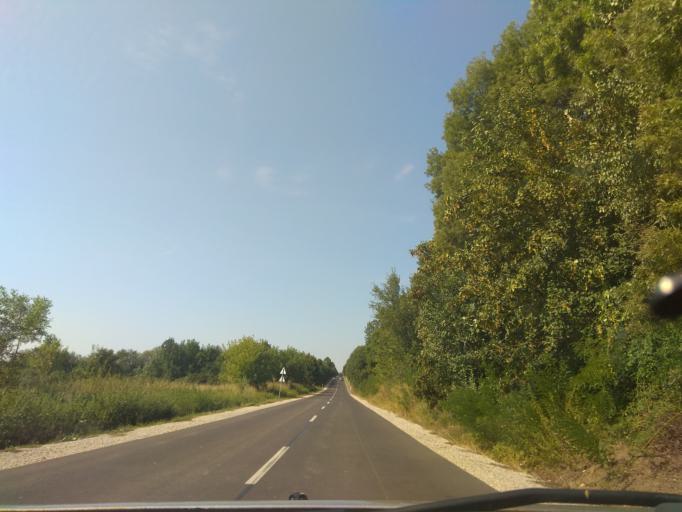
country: HU
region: Borsod-Abauj-Zemplen
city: Harsany
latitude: 47.9386
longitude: 20.7402
